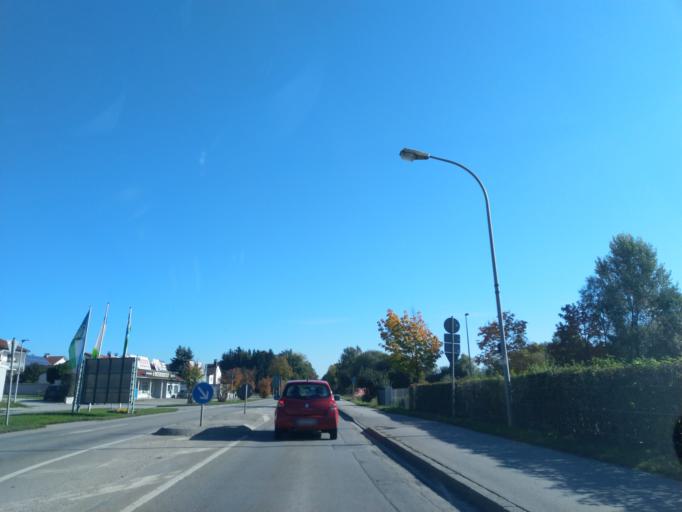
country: DE
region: Bavaria
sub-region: Lower Bavaria
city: Plattling
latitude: 48.7838
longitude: 12.8841
